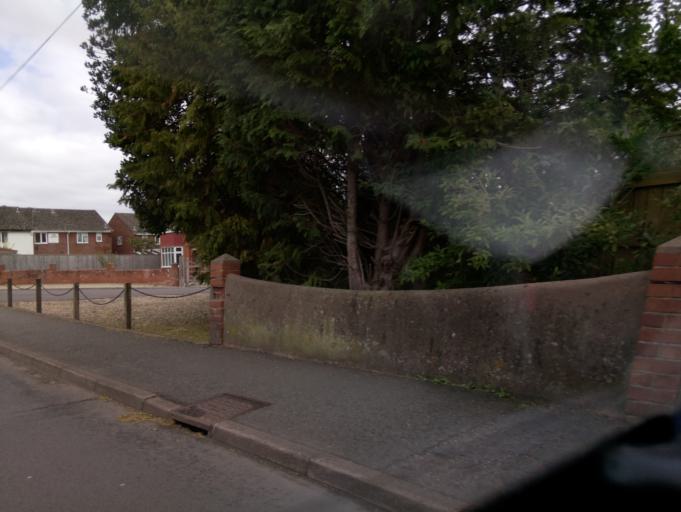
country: GB
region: England
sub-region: Devon
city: Cullompton
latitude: 50.8651
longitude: -3.3917
